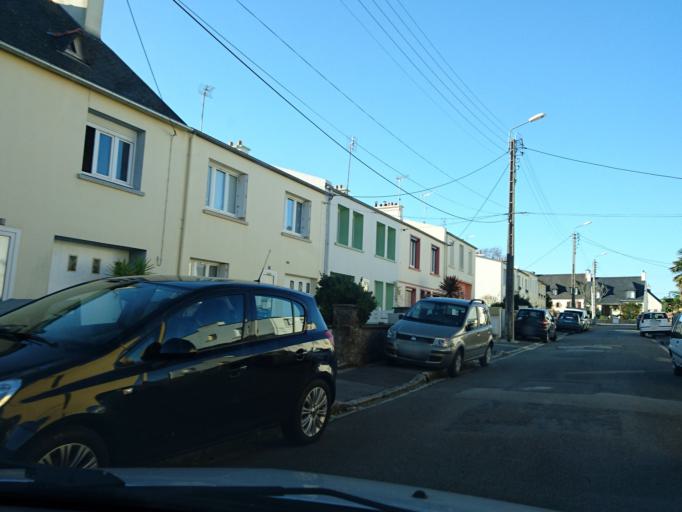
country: FR
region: Brittany
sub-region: Departement du Finistere
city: Brest
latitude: 48.4137
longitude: -4.4519
